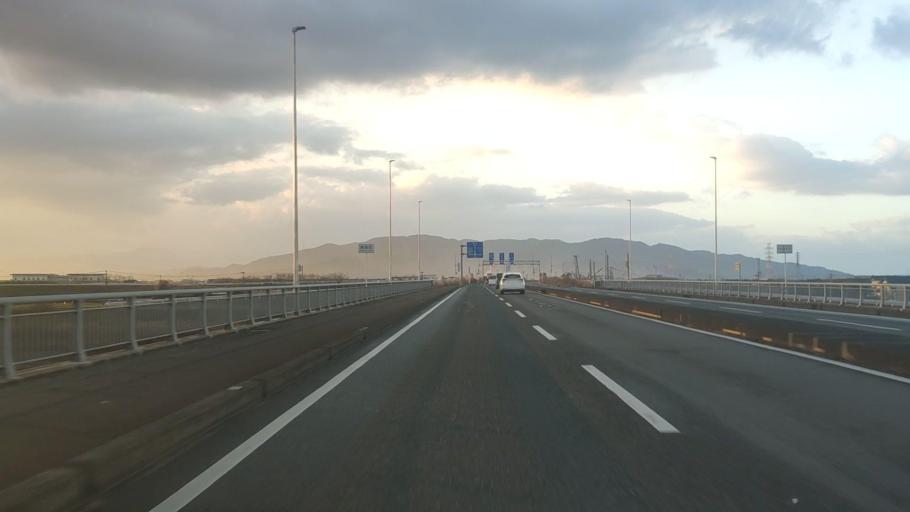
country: JP
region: Kumamoto
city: Kumamoto
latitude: 32.7406
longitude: 130.7047
